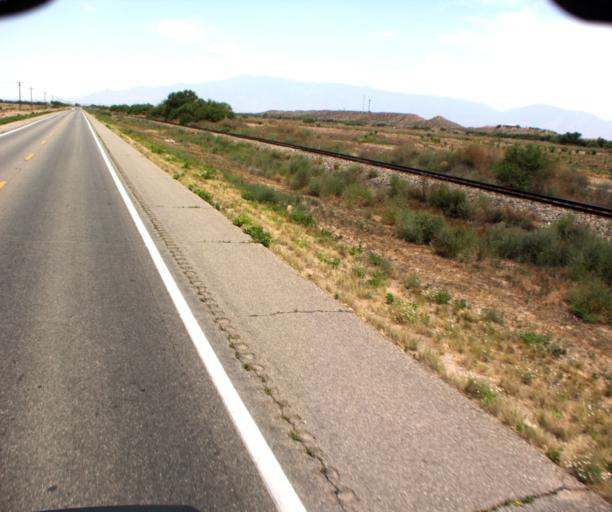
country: US
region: Arizona
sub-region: Graham County
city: Pima
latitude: 33.0072
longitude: -109.9471
